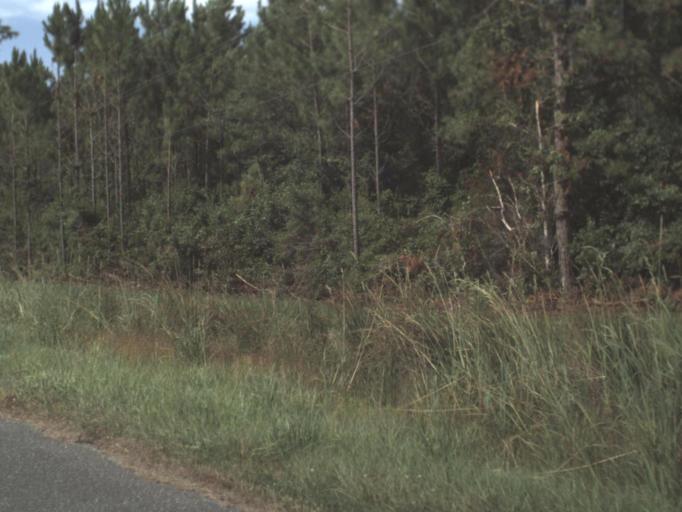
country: US
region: Florida
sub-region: Taylor County
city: Perry
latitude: 30.2577
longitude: -83.6244
